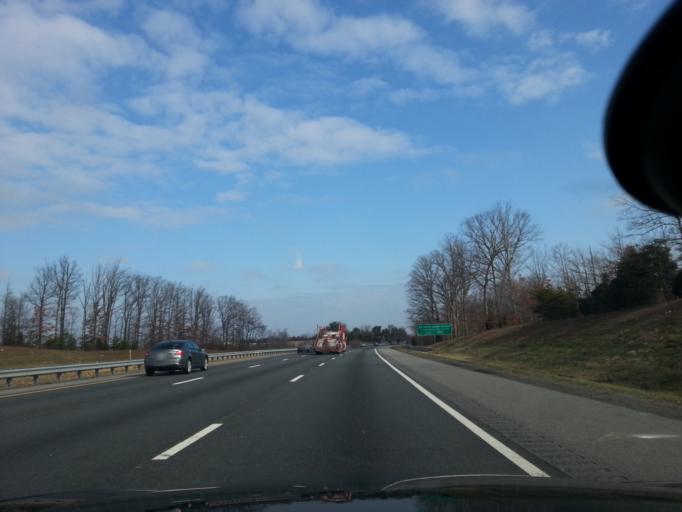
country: US
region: Virginia
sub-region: Spotsylvania County
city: Spotsylvania Courthouse
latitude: 38.2204
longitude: -77.4997
